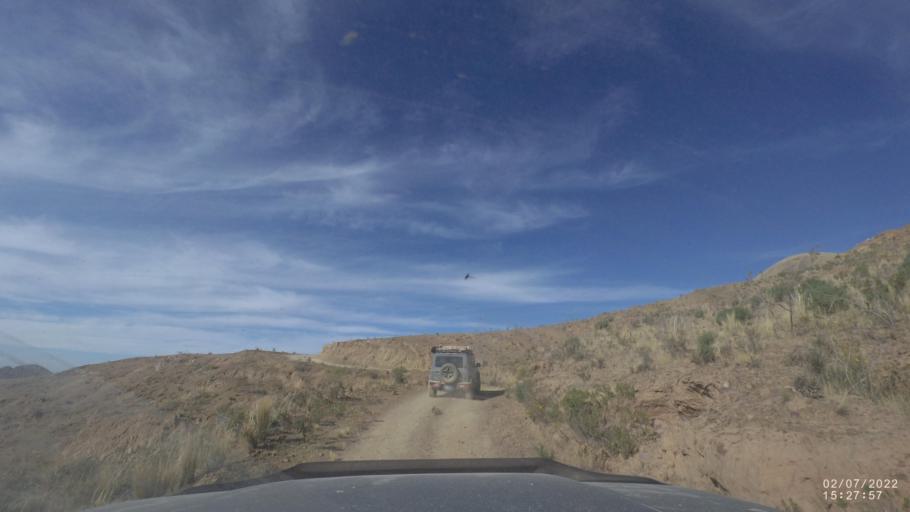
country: BO
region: Cochabamba
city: Irpa Irpa
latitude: -17.8778
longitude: -66.4141
